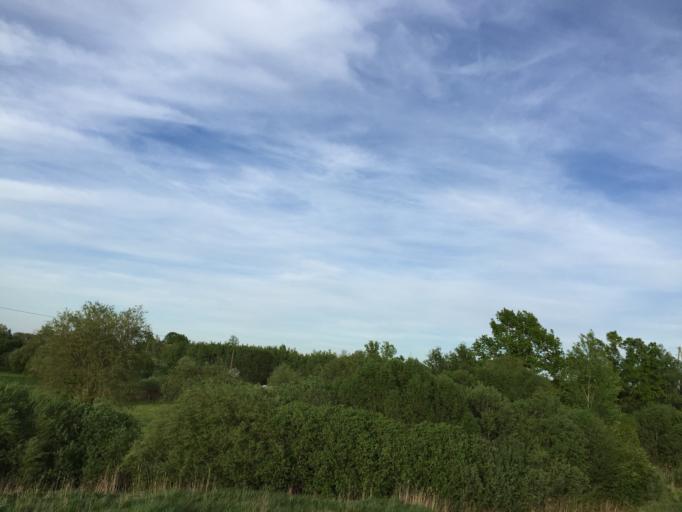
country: LV
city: Tireli
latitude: 56.6816
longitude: 23.4987
